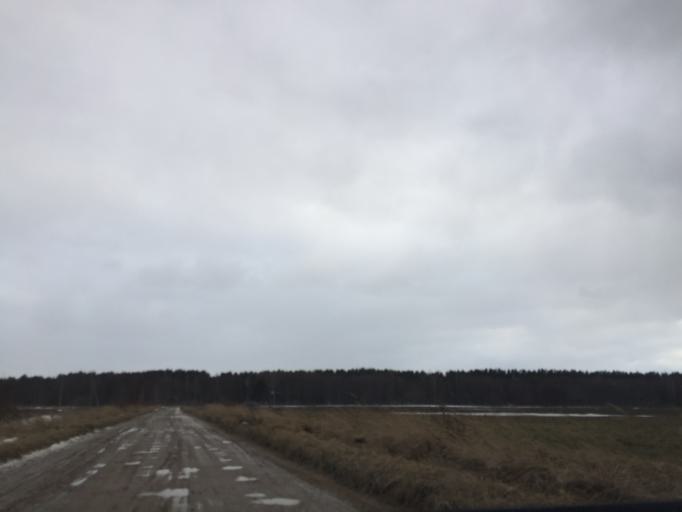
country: LV
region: Salacgrivas
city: Salacgriva
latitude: 57.6434
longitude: 24.3866
